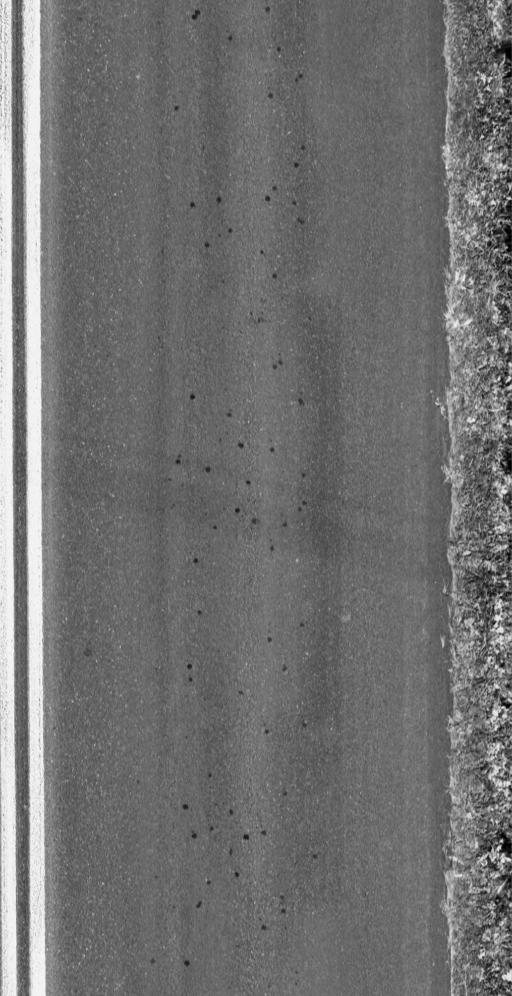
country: US
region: Vermont
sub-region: Bennington County
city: Arlington
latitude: 43.1379
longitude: -73.2040
